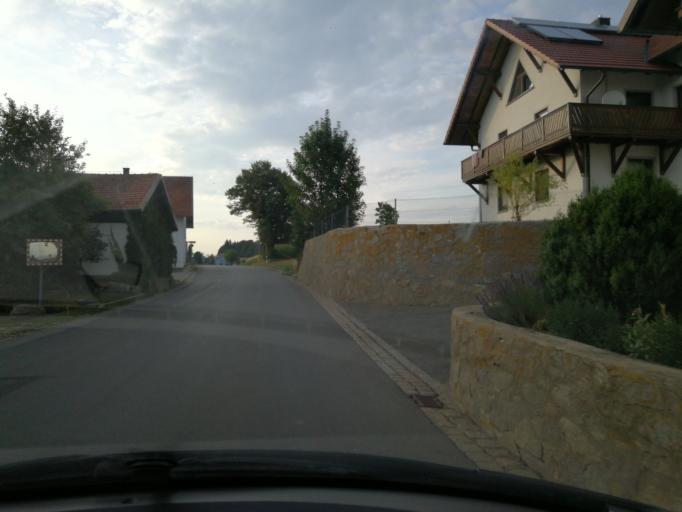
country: DE
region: Bavaria
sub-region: Lower Bavaria
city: Wiesenfelden
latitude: 49.0679
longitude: 12.5182
